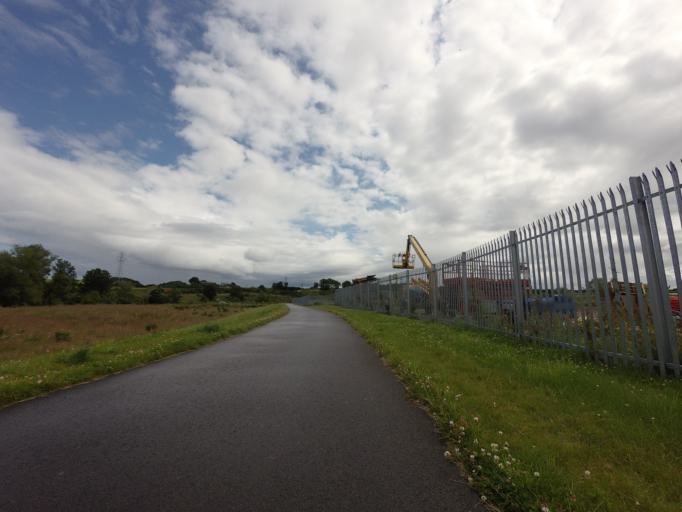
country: GB
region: Scotland
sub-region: Moray
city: Elgin
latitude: 57.6520
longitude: -3.2951
